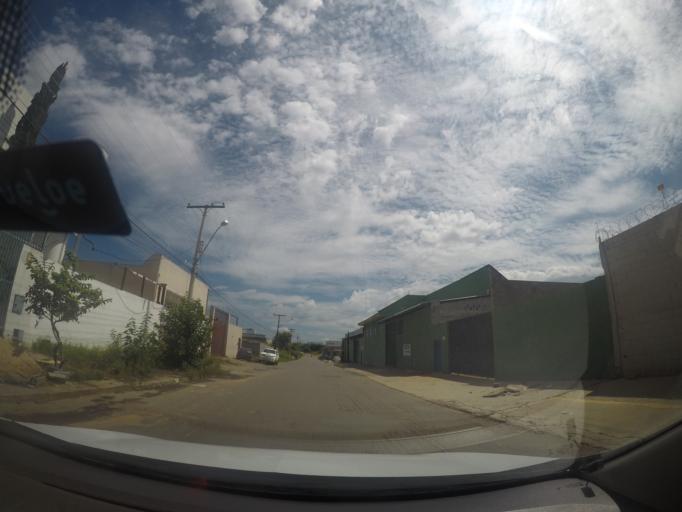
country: BR
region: Goias
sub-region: Goiania
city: Goiania
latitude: -16.6916
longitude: -49.3226
